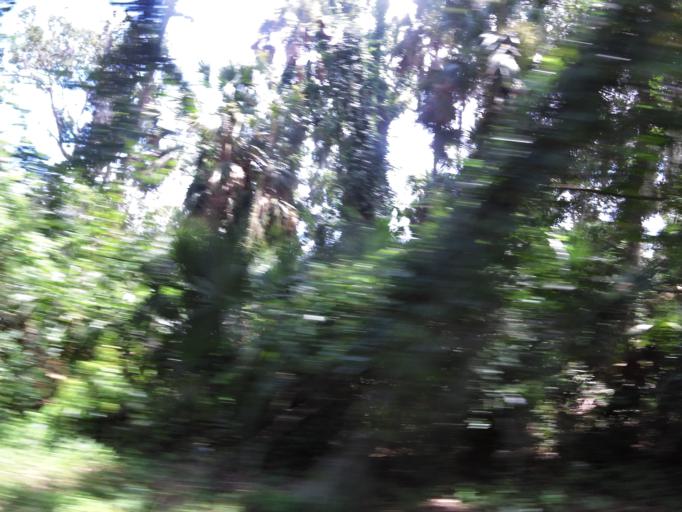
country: US
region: Florida
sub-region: Flagler County
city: Flagler Beach
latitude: 29.4039
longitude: -81.1409
